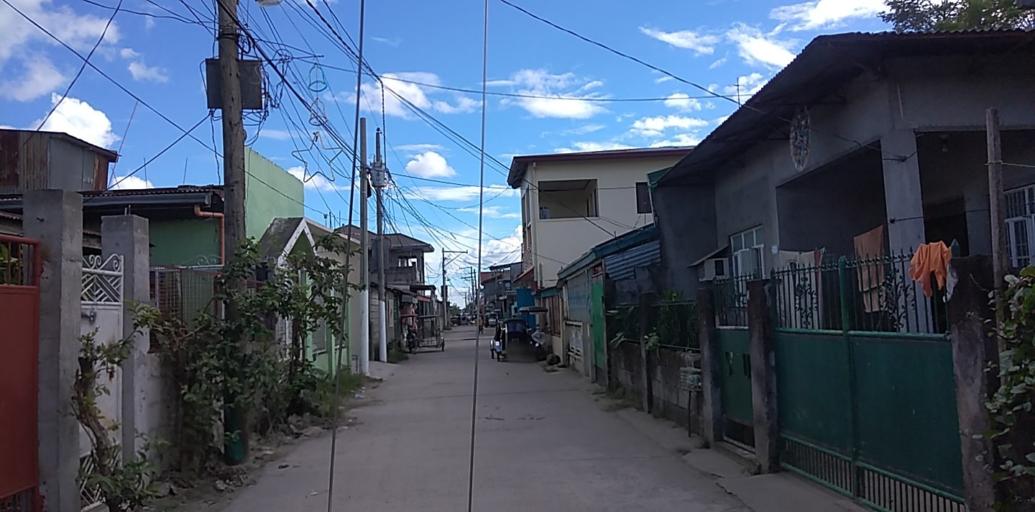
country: PH
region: Central Luzon
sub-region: Province of Pampanga
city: Arayat
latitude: 15.1398
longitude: 120.7697
